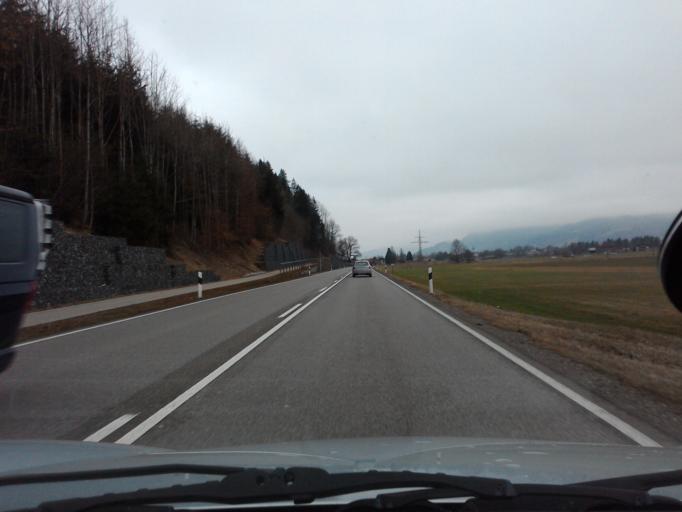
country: DE
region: Bavaria
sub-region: Swabia
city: Sonthofen
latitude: 47.4970
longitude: 10.2656
